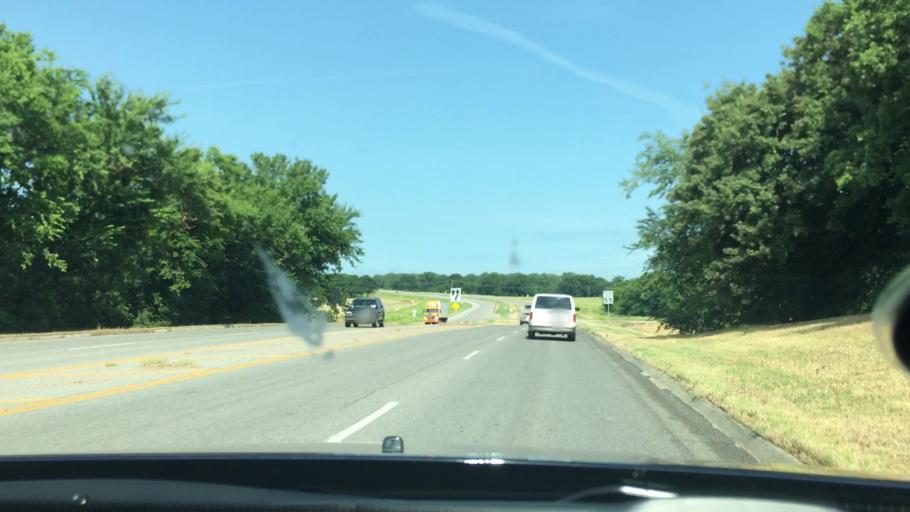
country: US
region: Oklahoma
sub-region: Murray County
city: Davis
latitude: 34.5028
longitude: -97.1284
